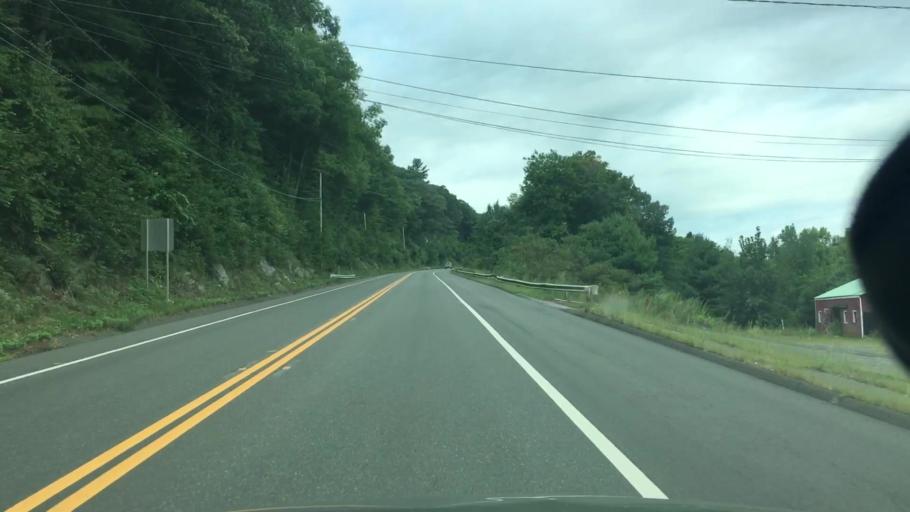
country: US
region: Massachusetts
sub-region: Franklin County
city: Greenfield
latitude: 42.5959
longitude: -72.6340
